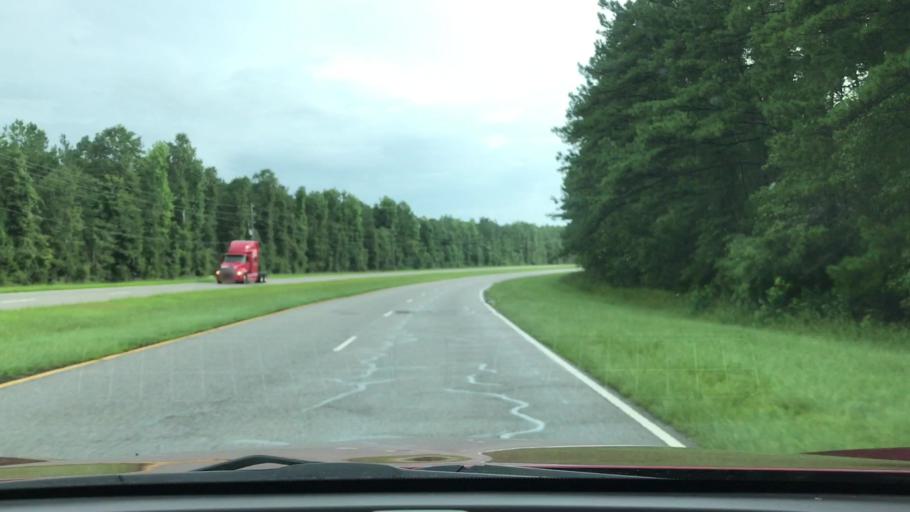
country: US
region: South Carolina
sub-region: Georgetown County
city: Georgetown
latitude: 33.2937
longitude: -79.3466
